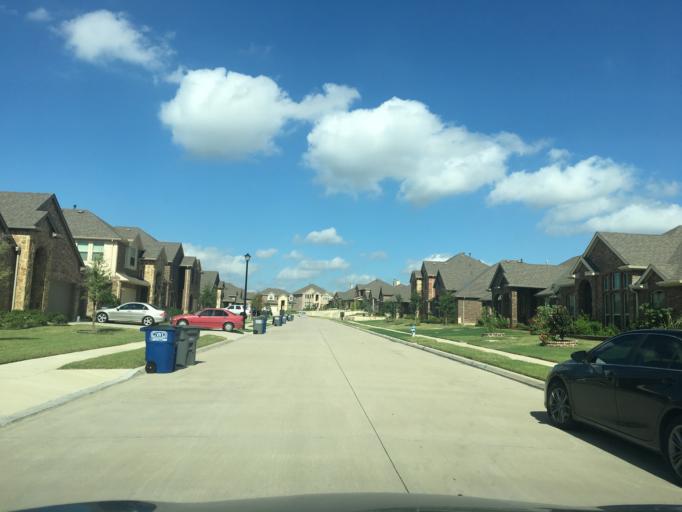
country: US
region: Texas
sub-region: Dallas County
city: Sachse
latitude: 32.9591
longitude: -96.5903
